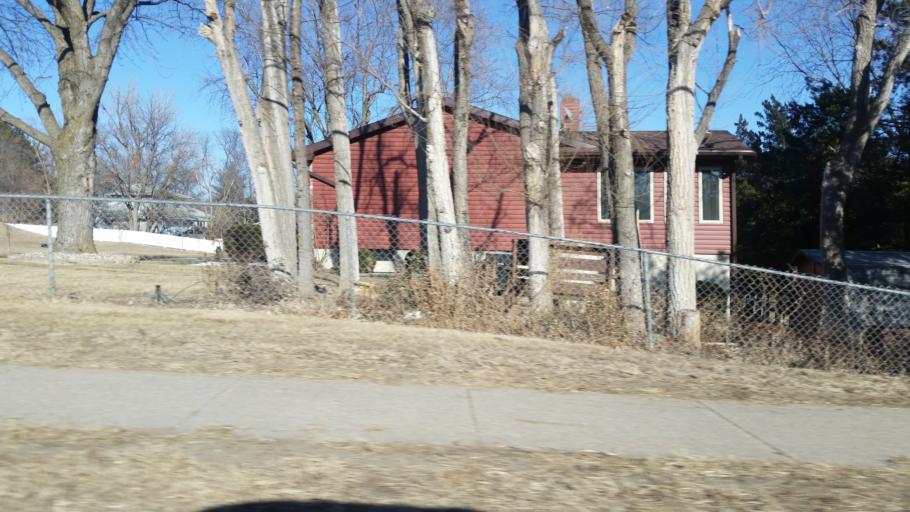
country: US
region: Nebraska
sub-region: Sarpy County
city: Bellevue
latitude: 41.1589
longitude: -95.9202
